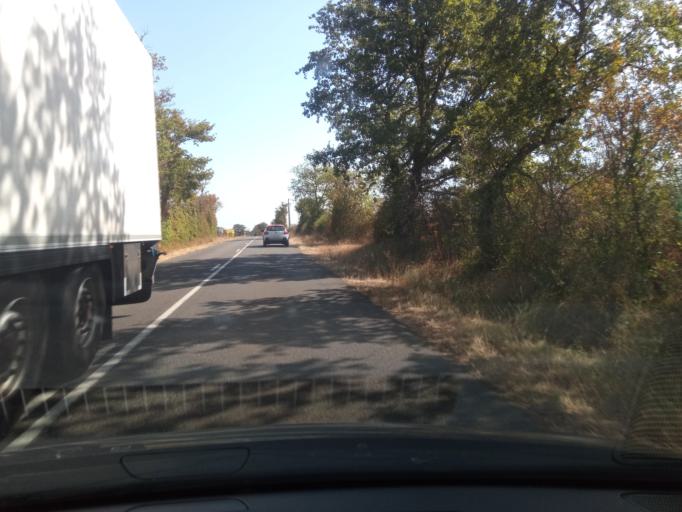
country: FR
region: Poitou-Charentes
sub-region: Departement de la Vienne
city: Montmorillon
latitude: 46.4342
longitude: 0.9055
